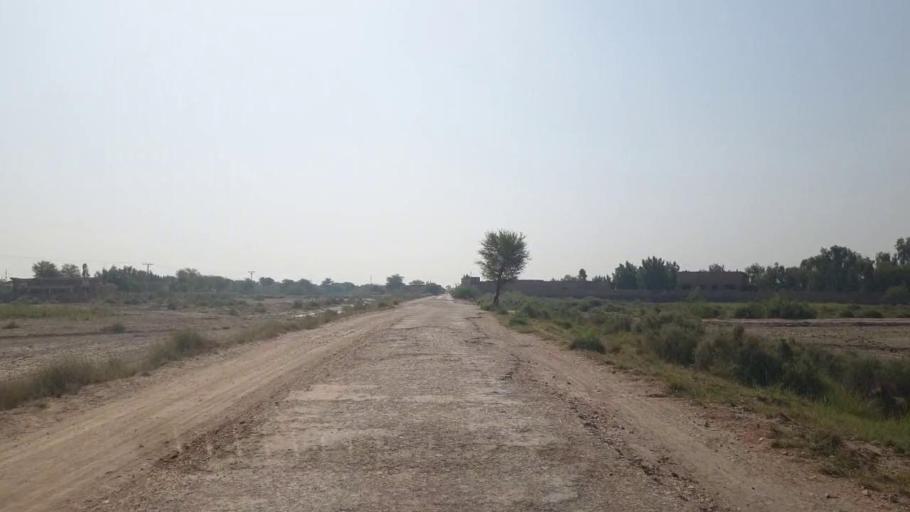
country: PK
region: Sindh
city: Berani
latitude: 25.8965
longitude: 68.7488
